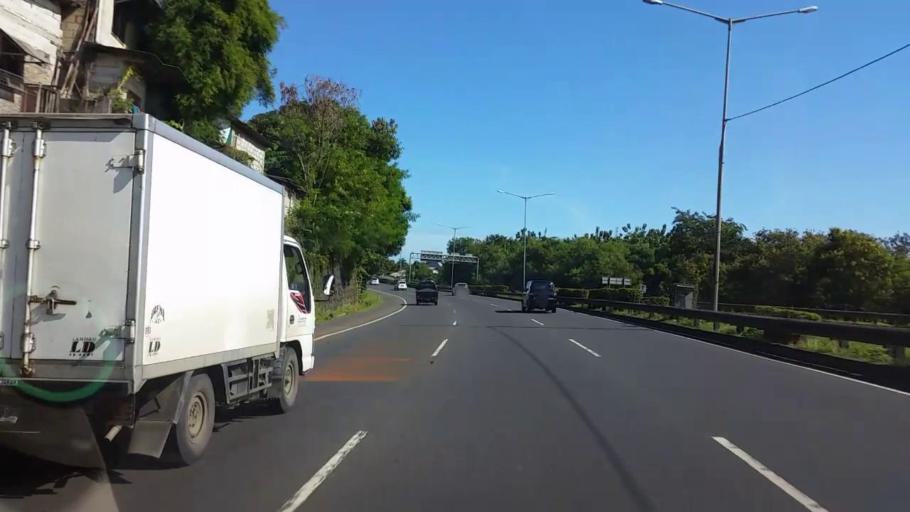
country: ID
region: Banten
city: South Tangerang
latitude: -6.2599
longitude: 106.7607
